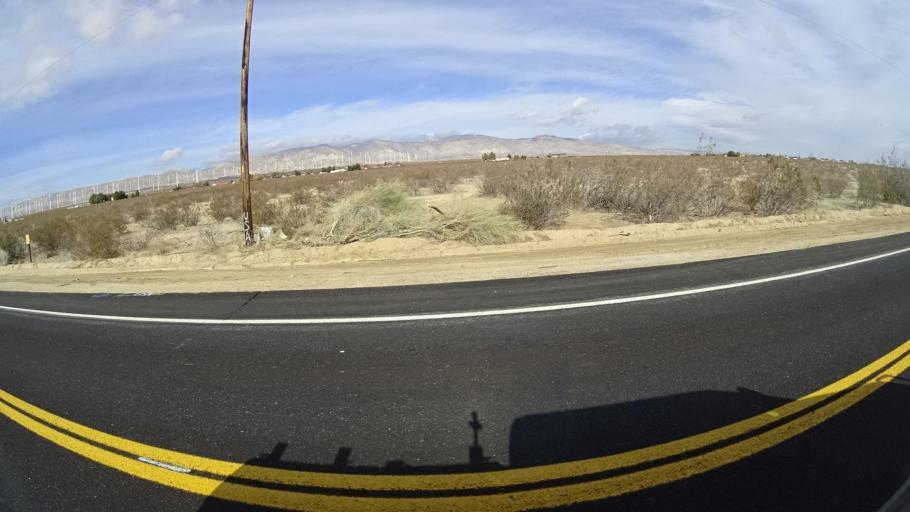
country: US
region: California
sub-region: Kern County
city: Mojave
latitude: 35.0549
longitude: -118.1884
